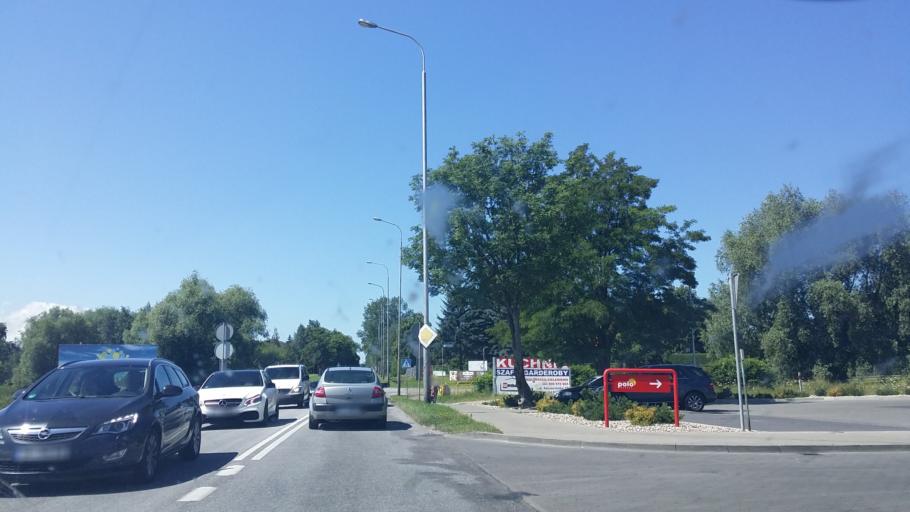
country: PL
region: West Pomeranian Voivodeship
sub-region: Powiat kolobrzeski
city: Kolobrzeg
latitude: 54.1617
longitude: 15.5419
